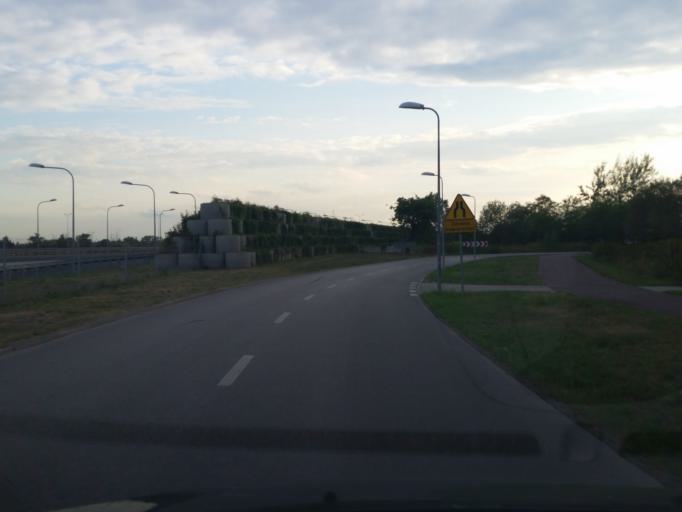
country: PL
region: Masovian Voivodeship
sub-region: Powiat piaseczynski
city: Mysiadlo
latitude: 52.1408
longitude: 20.9867
